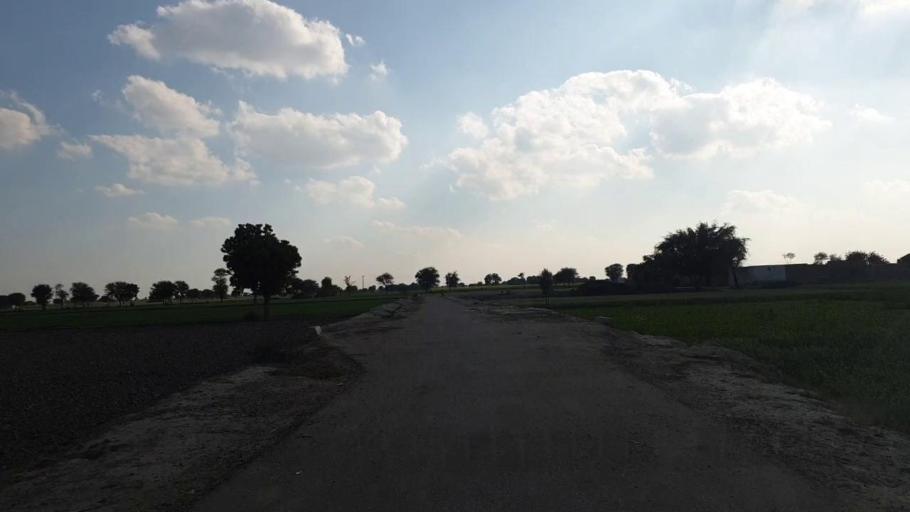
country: PK
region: Sindh
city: Shahpur Chakar
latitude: 26.1043
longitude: 68.5846
